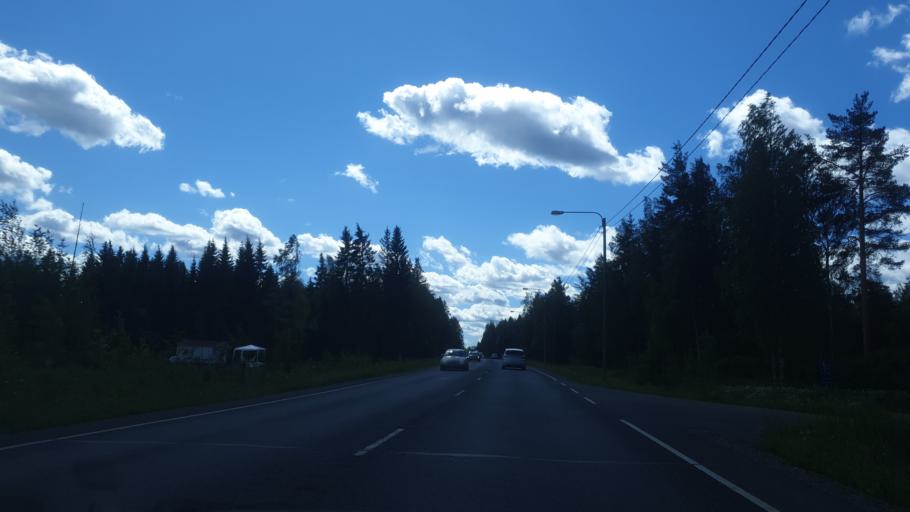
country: FI
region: Northern Savo
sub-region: Varkaus
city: Leppaevirta
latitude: 62.5922
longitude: 27.6052
